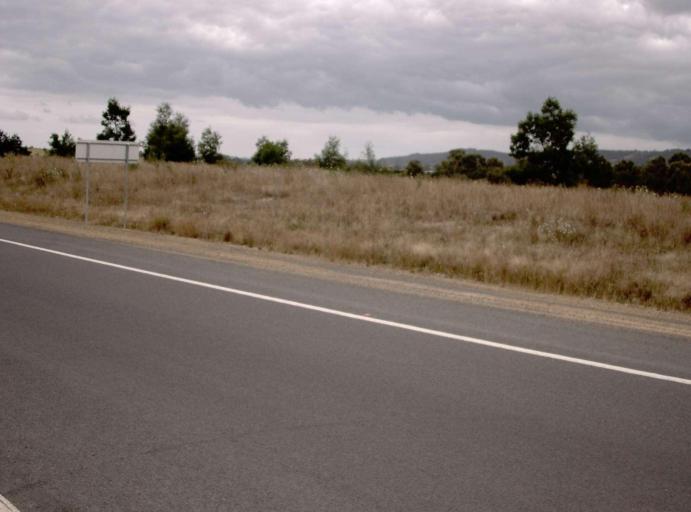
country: AU
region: Victoria
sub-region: Yarra Ranges
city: Yarra Glen
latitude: -37.6481
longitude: 145.3970
